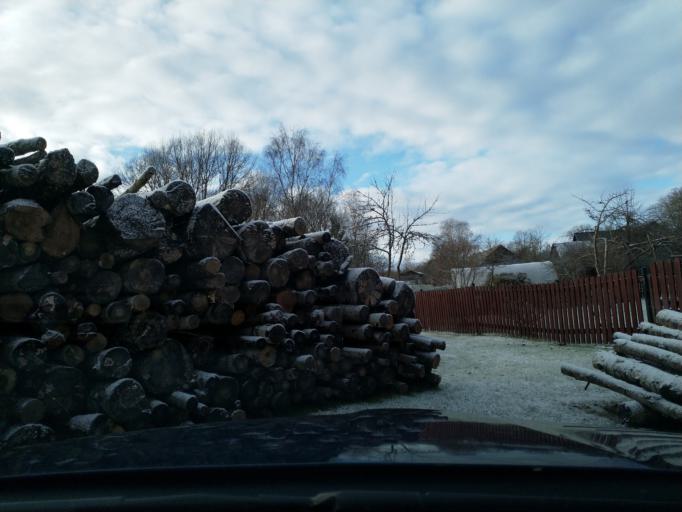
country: LV
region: Kuldigas Rajons
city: Kuldiga
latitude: 56.9650
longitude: 21.9438
